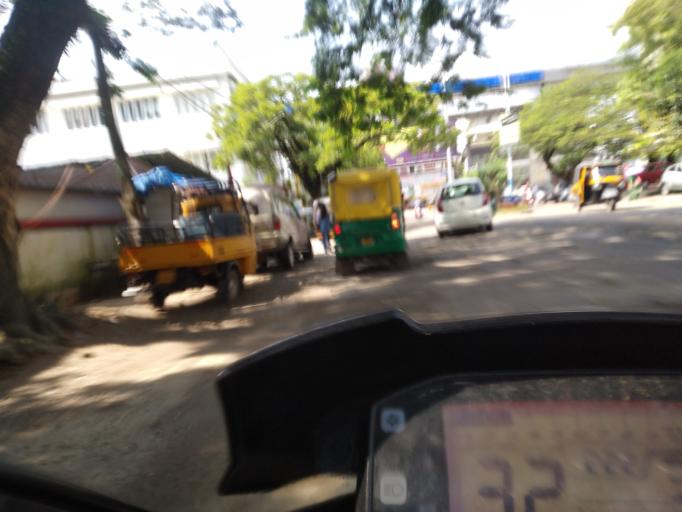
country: IN
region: Kerala
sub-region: Ernakulam
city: Cochin
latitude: 9.9649
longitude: 76.2950
